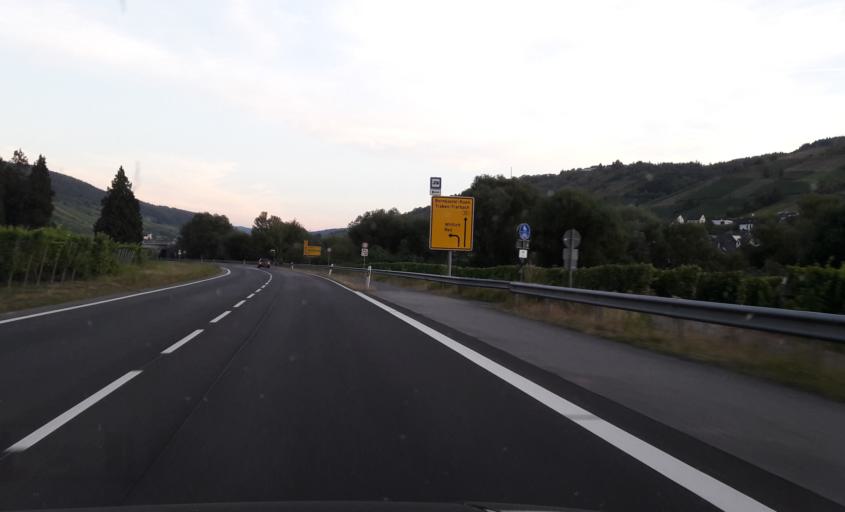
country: DE
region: Rheinland-Pfalz
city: Punderich
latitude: 50.0267
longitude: 7.1185
